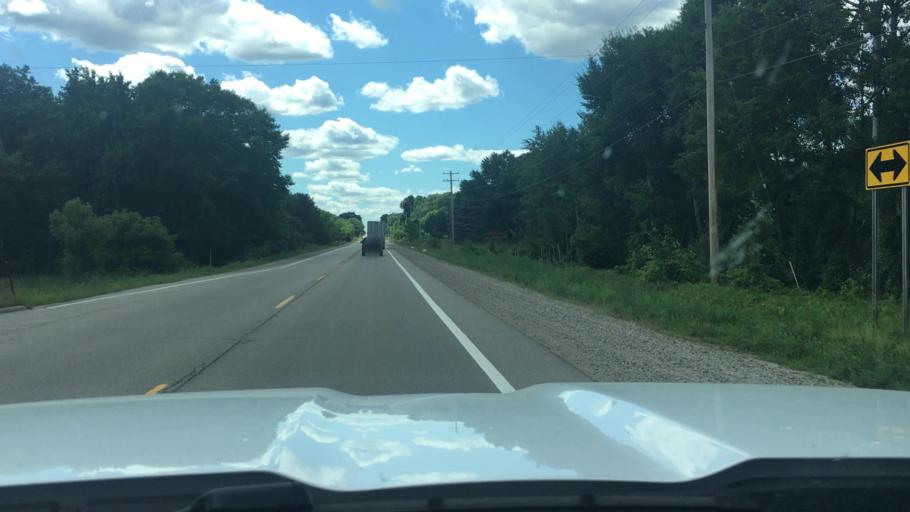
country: US
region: Michigan
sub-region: Montcalm County
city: Greenville
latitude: 43.1764
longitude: -85.3823
